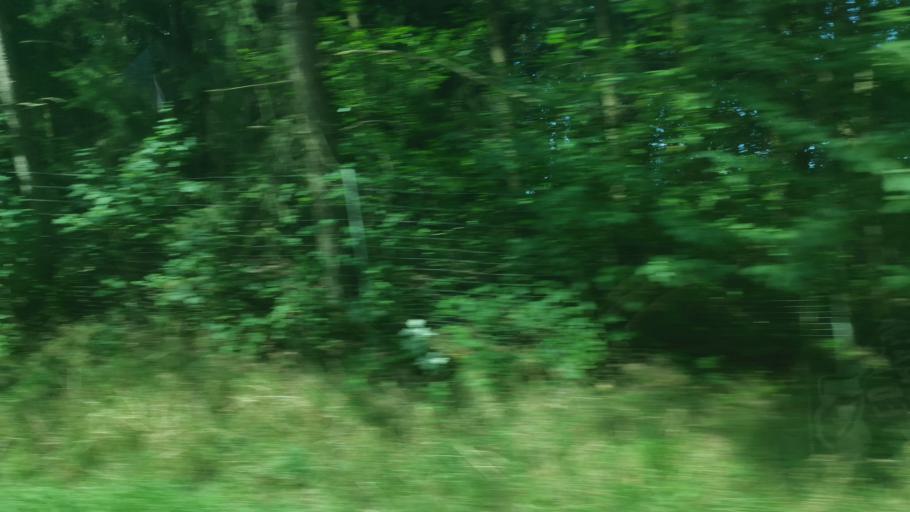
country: DE
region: Bavaria
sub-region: Upper Palatinate
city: Pemfling
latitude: 49.2661
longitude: 12.6311
